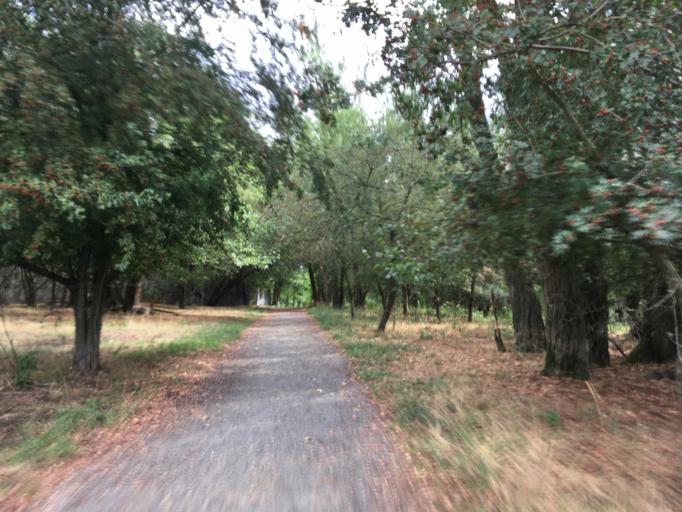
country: DE
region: Berlin
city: Staaken
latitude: 52.5202
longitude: 13.1377
